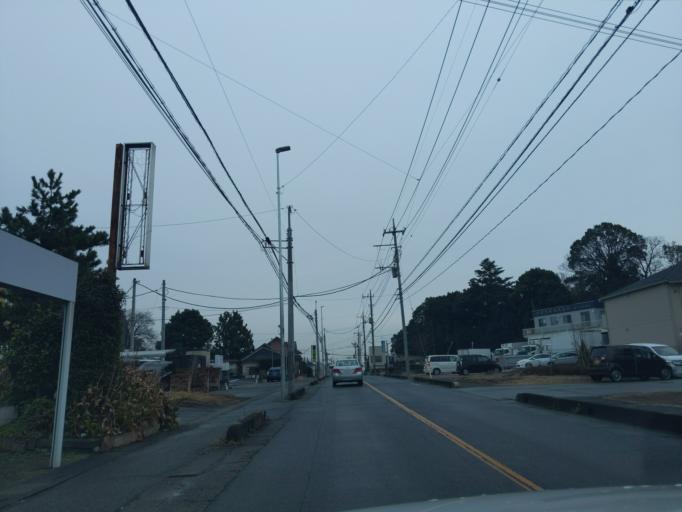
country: JP
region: Saitama
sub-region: Kawaguchi-shi
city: Hatogaya-honcho
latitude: 35.8604
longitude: 139.7414
